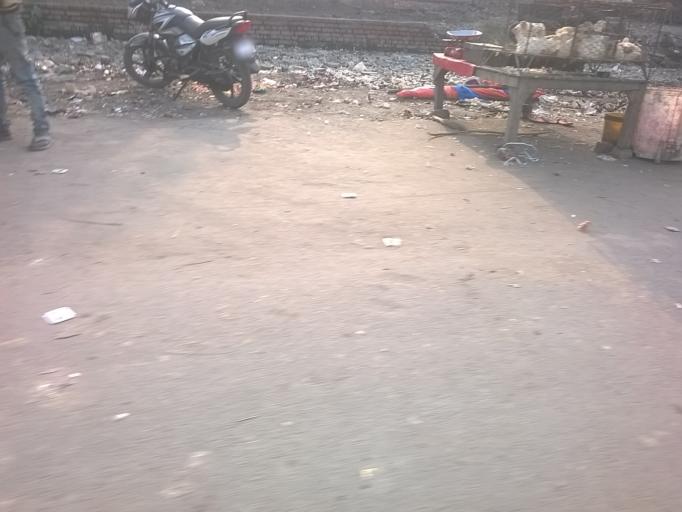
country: IN
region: Uttar Pradesh
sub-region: Kanpur
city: Kanpur
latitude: 26.4408
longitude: 80.3233
